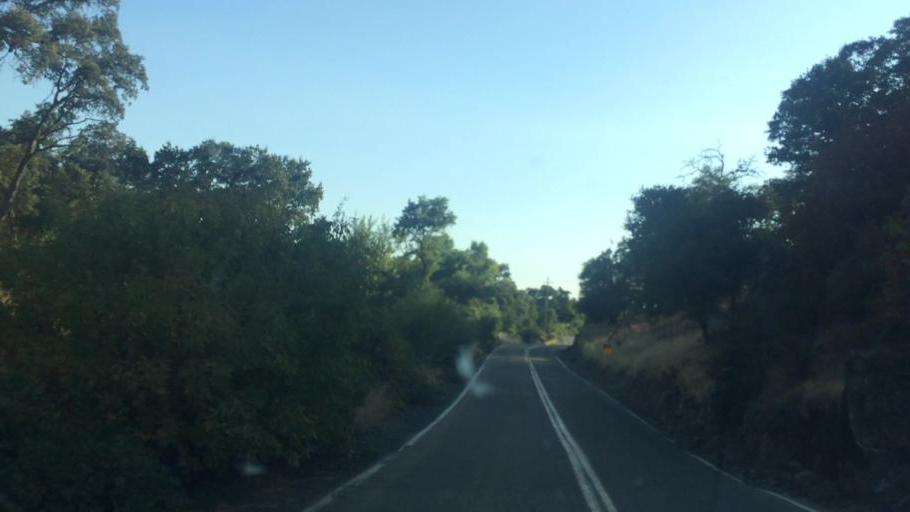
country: US
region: California
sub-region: Amador County
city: Plymouth
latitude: 38.4840
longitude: -120.8842
